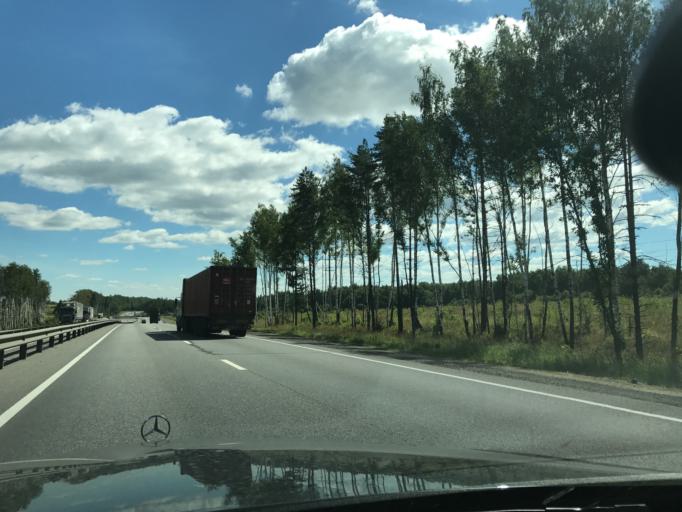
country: RU
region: Vladimir
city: Novovyazniki
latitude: 56.1959
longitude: 42.3723
